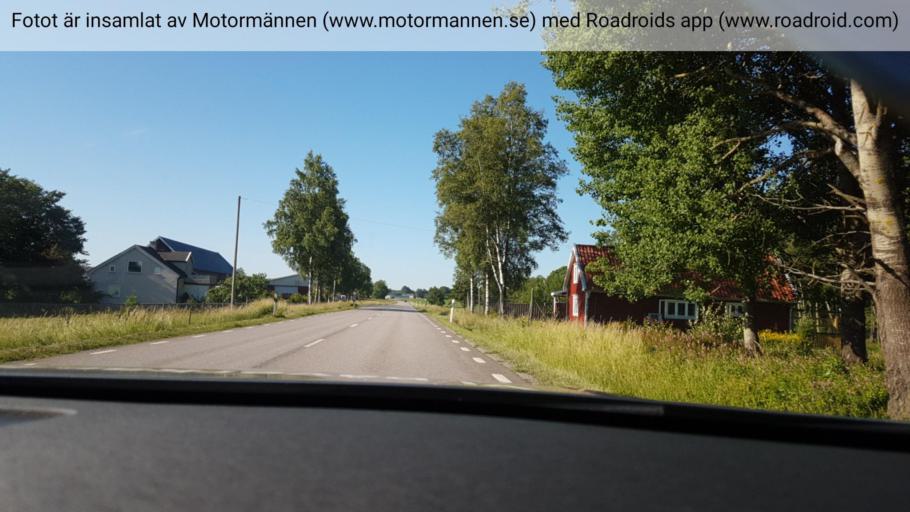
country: SE
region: Vaestra Goetaland
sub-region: Falkopings Kommun
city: Falkoeping
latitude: 58.0979
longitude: 13.5281
